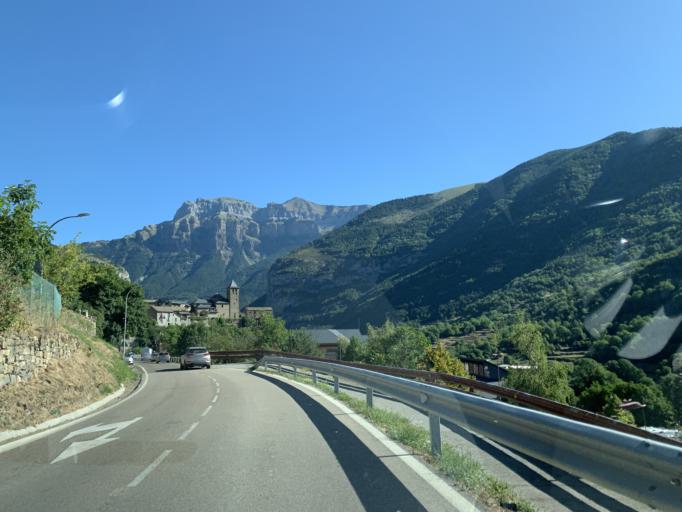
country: ES
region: Aragon
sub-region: Provincia de Huesca
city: Broto
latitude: 42.6248
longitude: -0.1121
